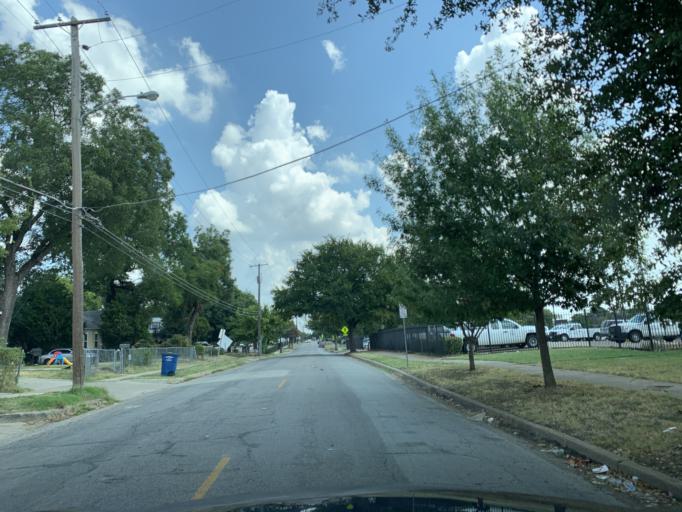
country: US
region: Texas
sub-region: Dallas County
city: Dallas
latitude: 32.7428
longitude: -96.8206
